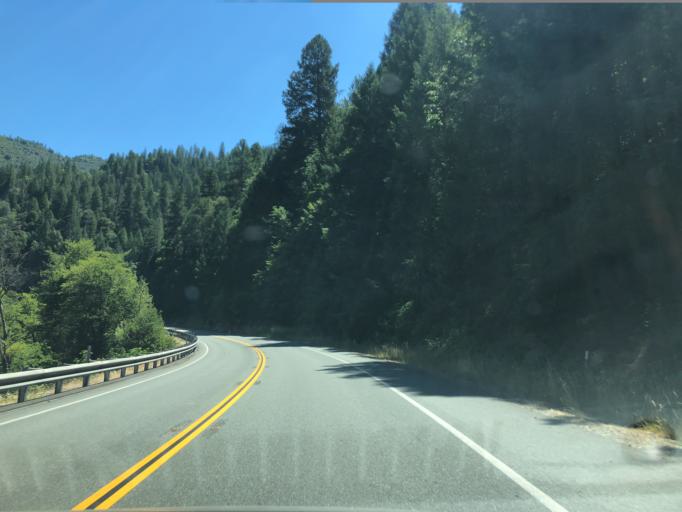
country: US
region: California
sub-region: Trinity County
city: Weaverville
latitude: 40.6531
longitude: -122.9013
